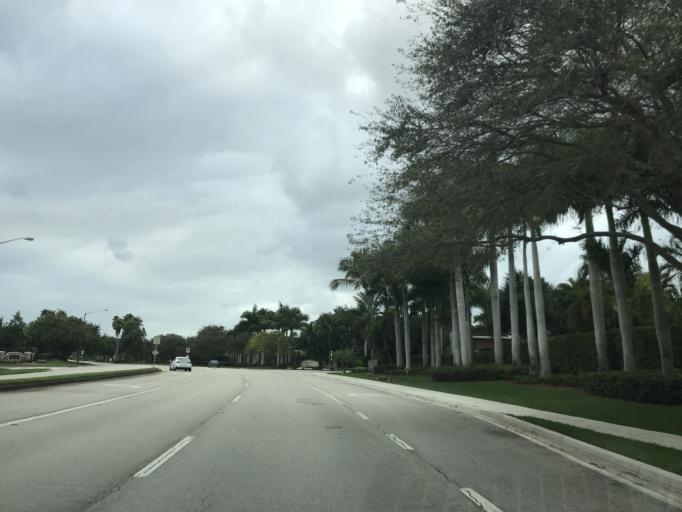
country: US
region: Florida
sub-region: Broward County
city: Coral Springs
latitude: 26.2998
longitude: -80.2711
